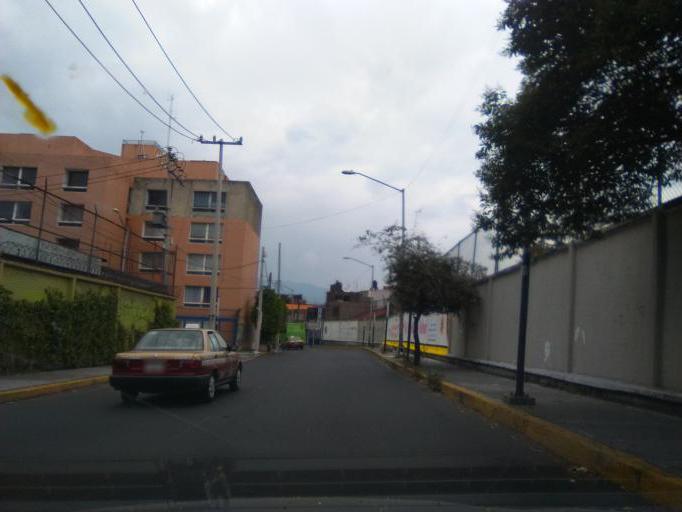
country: MX
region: Mexico City
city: Alvaro Obregon
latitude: 19.3701
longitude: -99.2236
